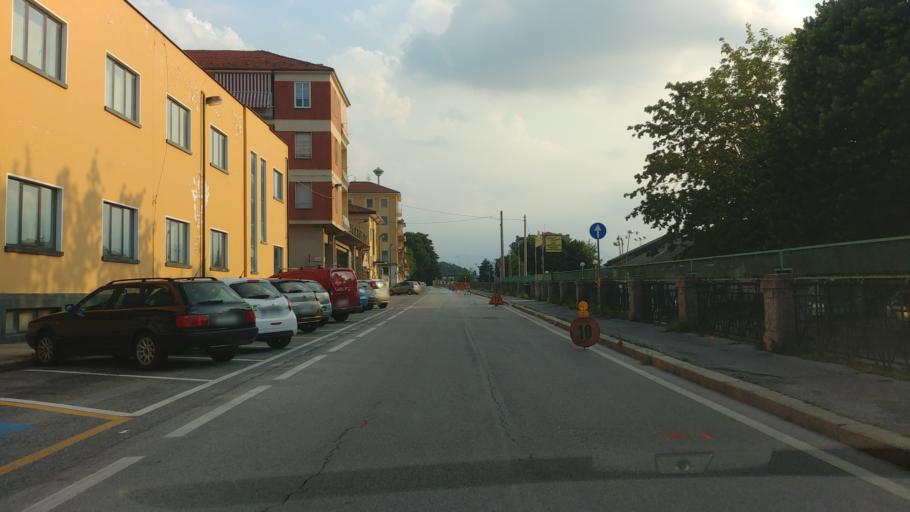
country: IT
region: Piedmont
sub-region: Provincia di Cuneo
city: Cuneo
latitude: 44.3901
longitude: 7.5398
